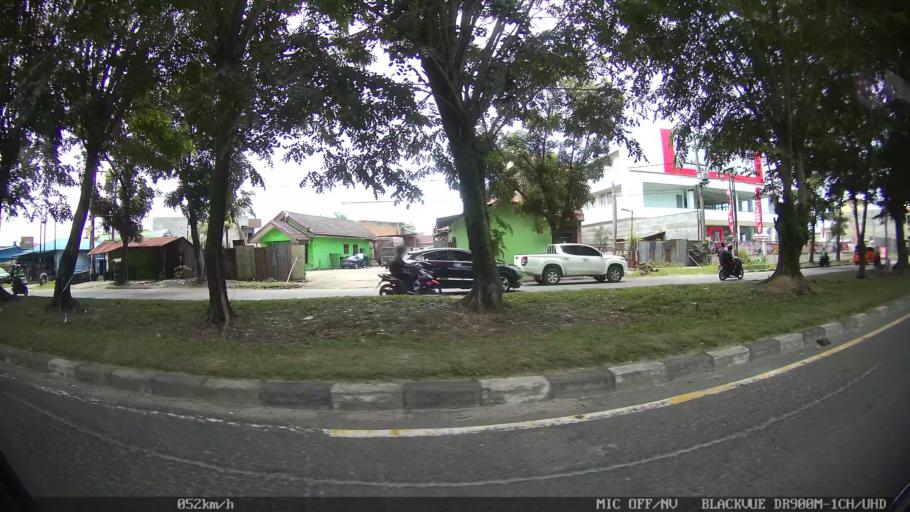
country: ID
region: North Sumatra
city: Sunggal
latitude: 3.5406
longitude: 98.6439
